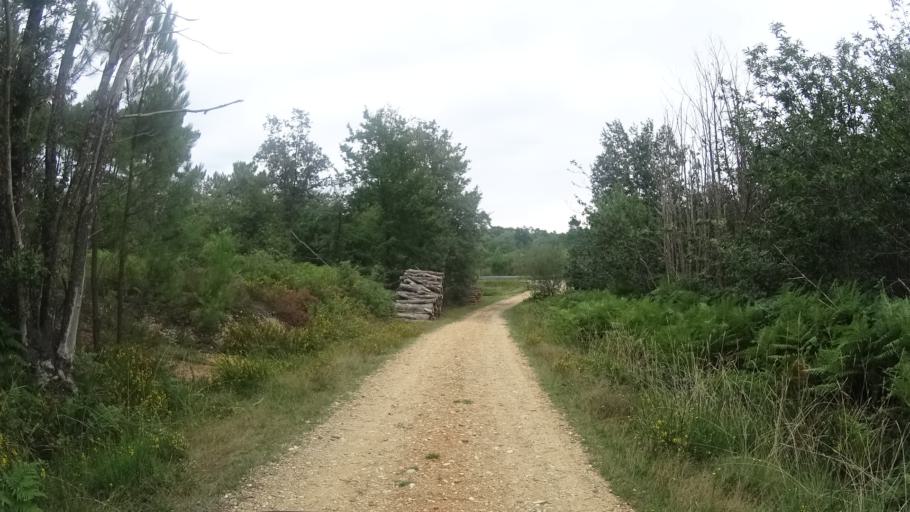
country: FR
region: Aquitaine
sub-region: Departement de la Dordogne
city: Sourzac
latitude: 45.0333
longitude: 0.3987
